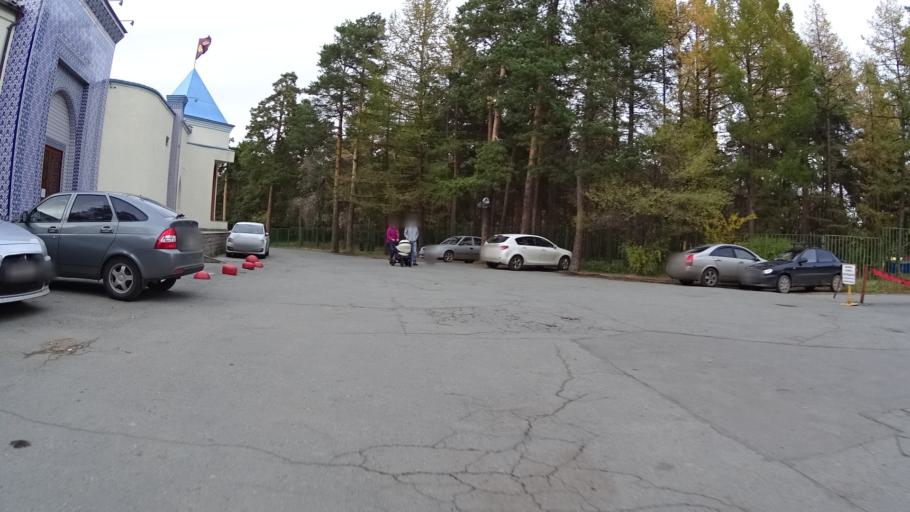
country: RU
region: Chelyabinsk
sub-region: Gorod Chelyabinsk
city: Chelyabinsk
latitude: 55.1655
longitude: 61.3664
